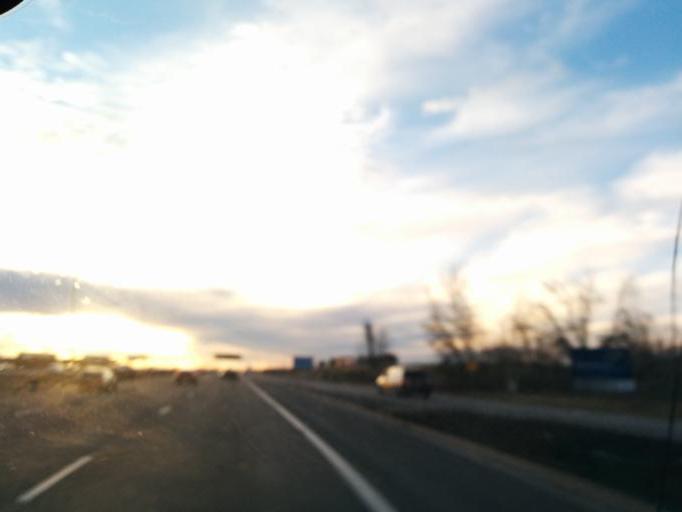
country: CA
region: Ontario
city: Etobicoke
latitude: 43.6674
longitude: -79.5962
